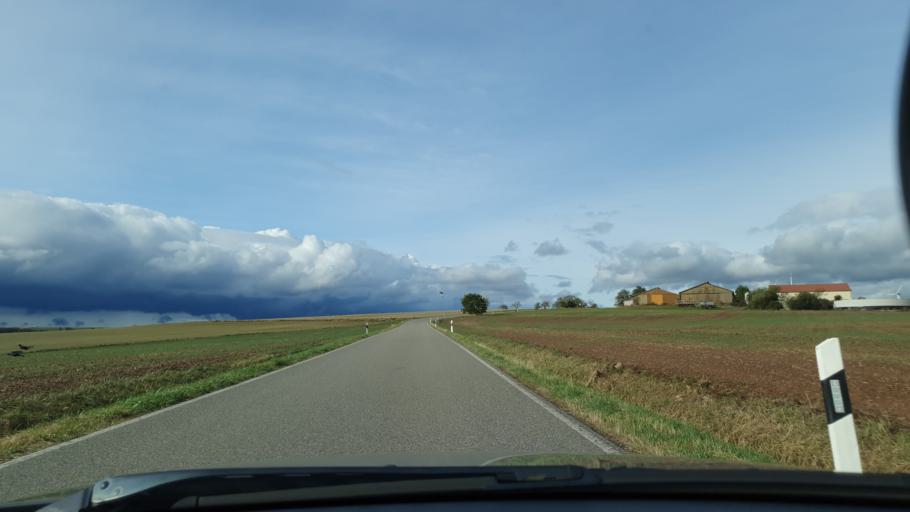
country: DE
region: Rheinland-Pfalz
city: Gerhardsbrunn
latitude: 49.3483
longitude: 7.5184
